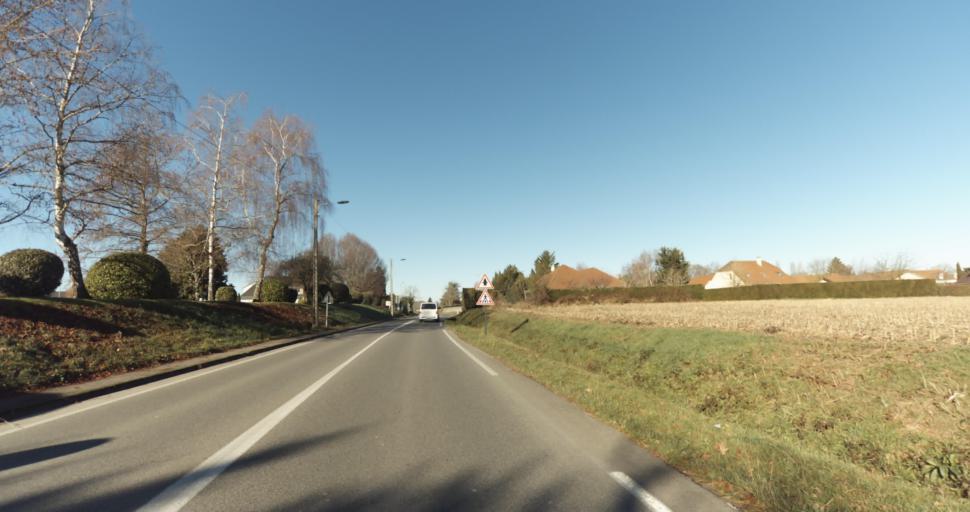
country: FR
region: Aquitaine
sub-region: Departement des Pyrenees-Atlantiques
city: Morlaas
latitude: 43.3513
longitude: -0.2644
